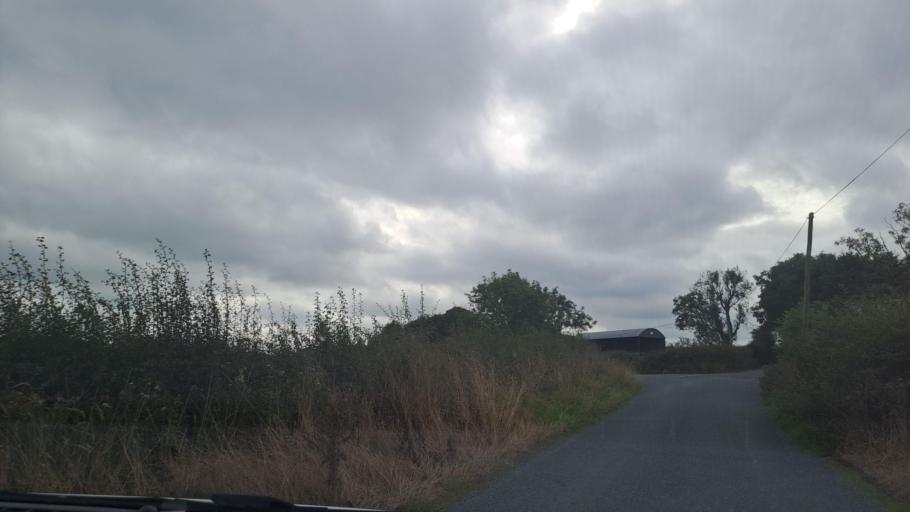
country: IE
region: Ulster
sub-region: An Cabhan
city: Bailieborough
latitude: 53.9511
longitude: -6.8939
